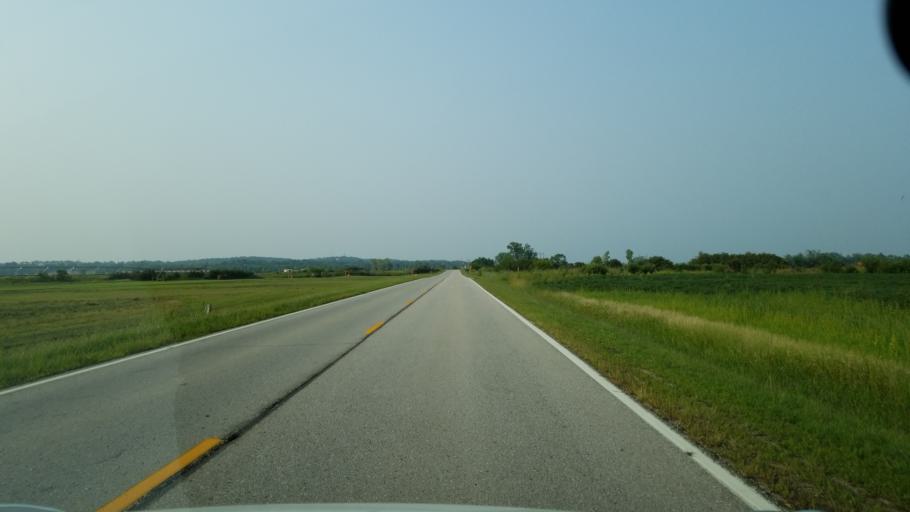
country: US
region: Nebraska
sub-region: Sarpy County
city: Bellevue
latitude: 41.1060
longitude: -95.8899
